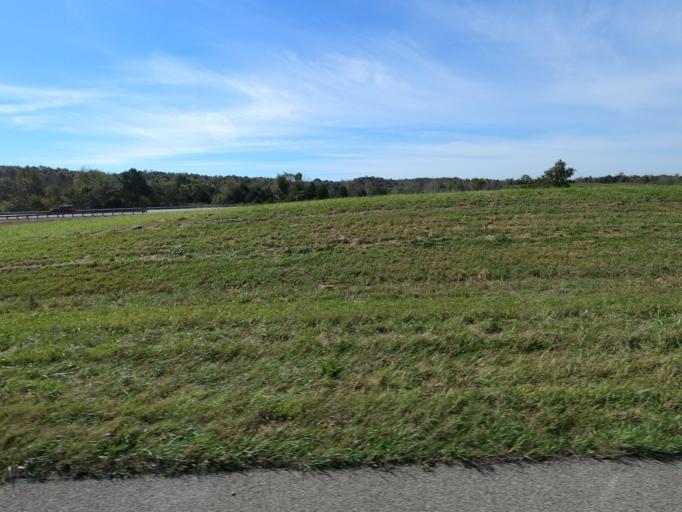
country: US
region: Tennessee
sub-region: Dickson County
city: Burns
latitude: 36.0194
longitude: -87.2564
